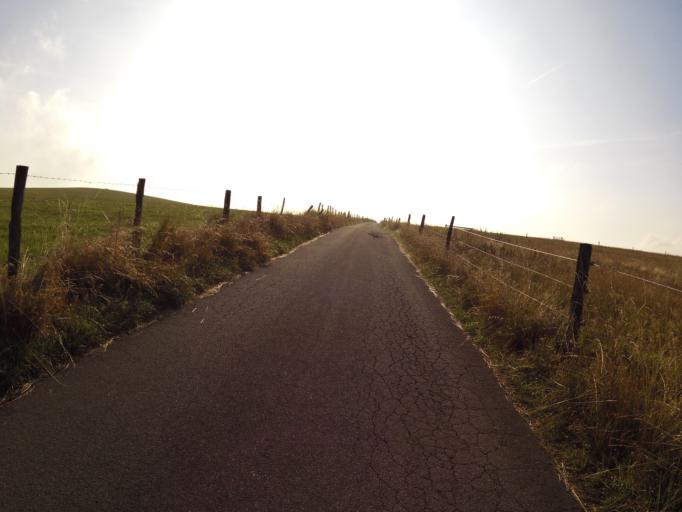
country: DE
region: North Rhine-Westphalia
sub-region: Regierungsbezirk Koln
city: Nettersheim
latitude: 50.4746
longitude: 6.6037
